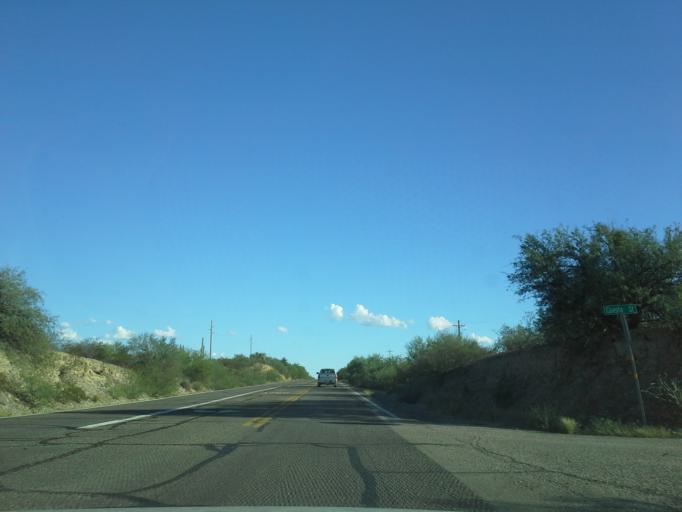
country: US
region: Arizona
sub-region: Pinal County
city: Mammoth
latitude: 32.7921
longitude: -110.6737
